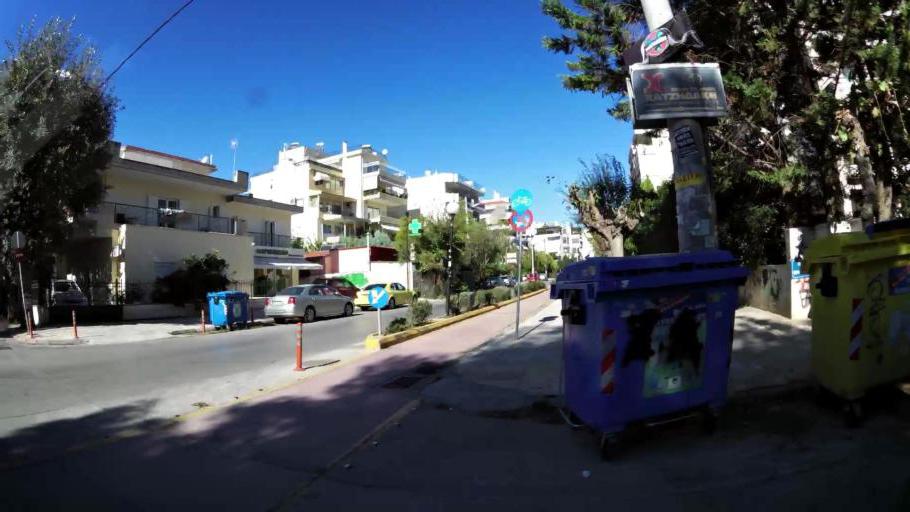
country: GR
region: Attica
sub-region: Nomarchia Athinas
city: Khalandrion
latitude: 38.0230
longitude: 23.8151
